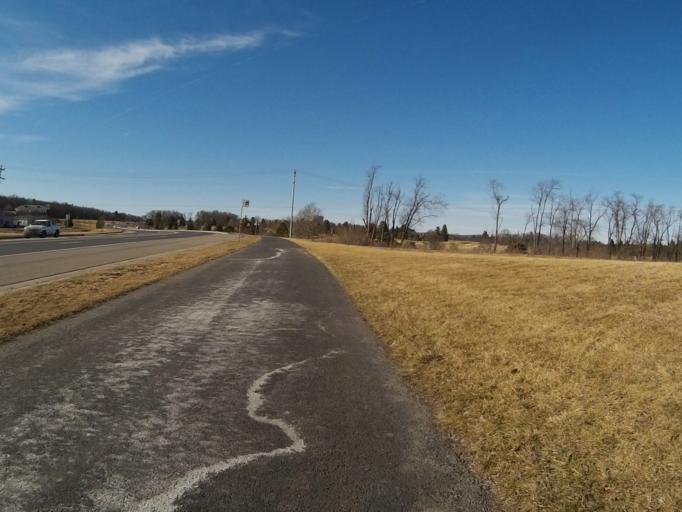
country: US
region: Pennsylvania
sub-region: Centre County
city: State College
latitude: 40.7807
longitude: -77.8811
